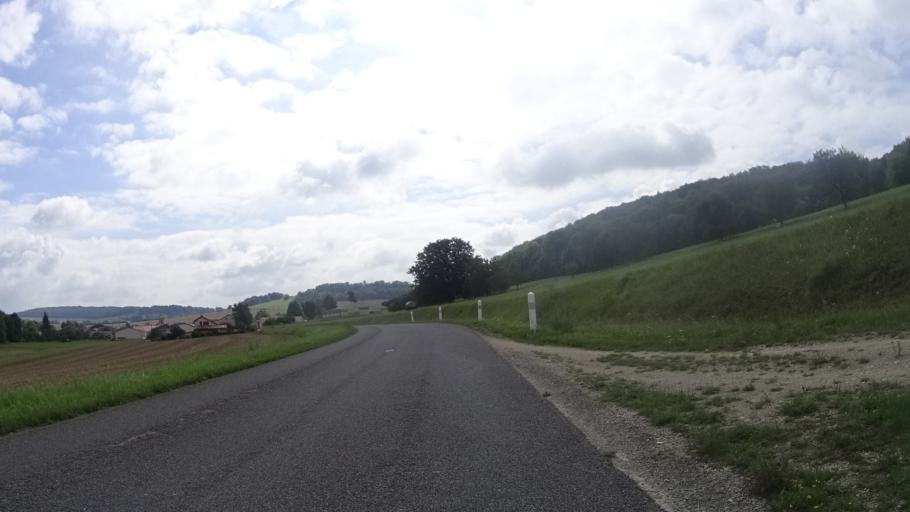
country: FR
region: Lorraine
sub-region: Departement de la Meuse
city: Ligny-en-Barrois
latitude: 48.7165
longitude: 5.3594
